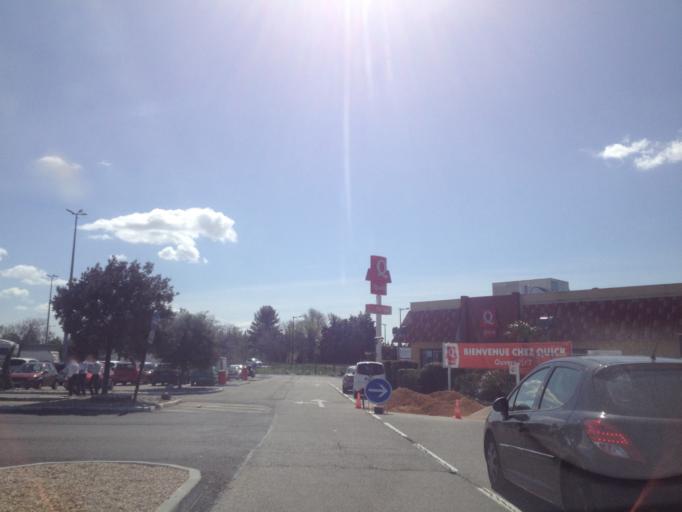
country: FR
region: Provence-Alpes-Cote d'Azur
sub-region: Departement du Vaucluse
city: Avignon
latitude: 43.9277
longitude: 4.7907
